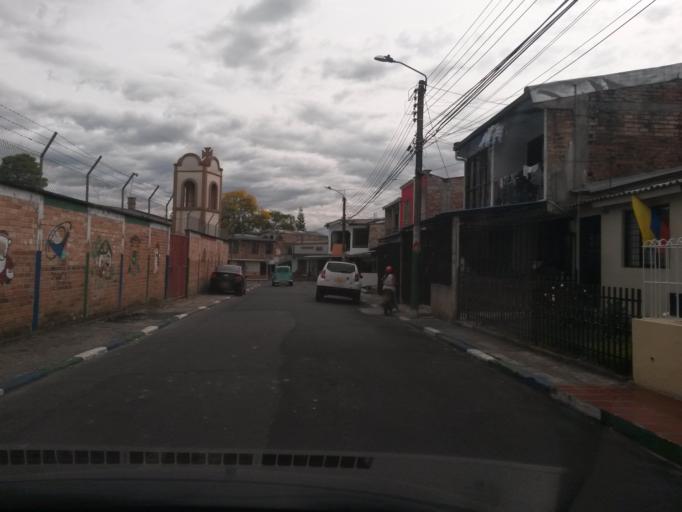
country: CO
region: Cauca
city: Popayan
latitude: 2.4472
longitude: -76.6164
